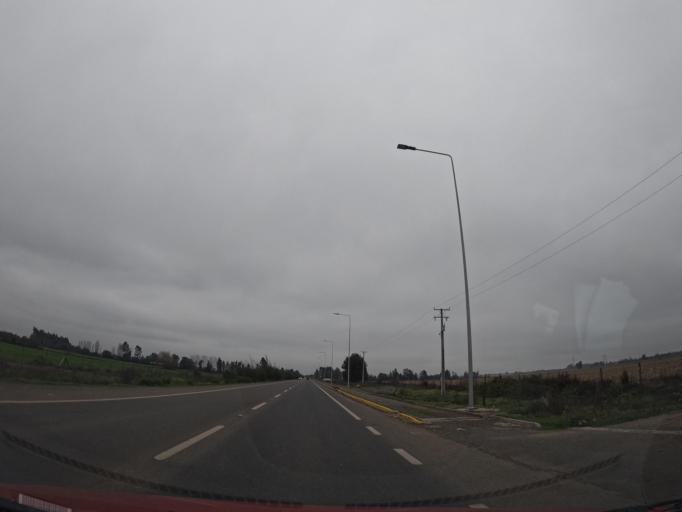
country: CL
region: Maule
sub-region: Provincia de Talca
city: San Clemente
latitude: -35.5178
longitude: -71.4956
